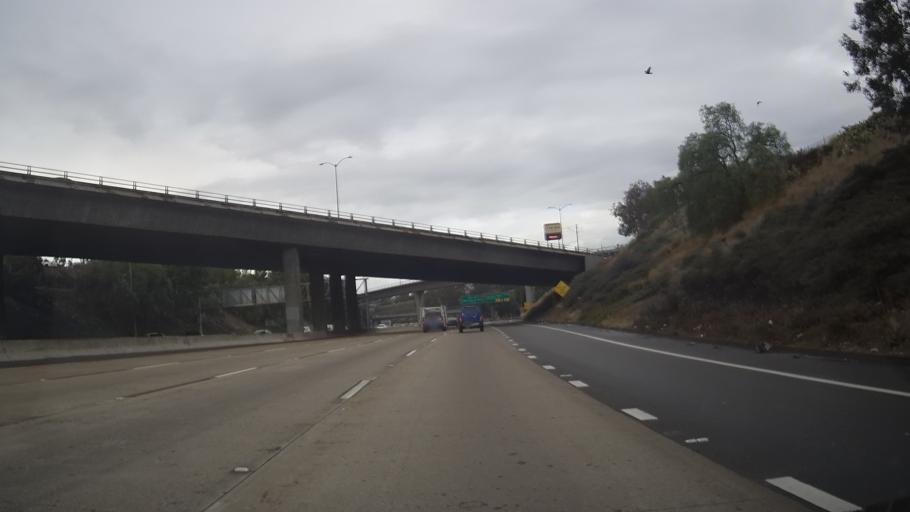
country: US
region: California
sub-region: San Diego County
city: La Mesa
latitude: 32.7718
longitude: -117.0258
